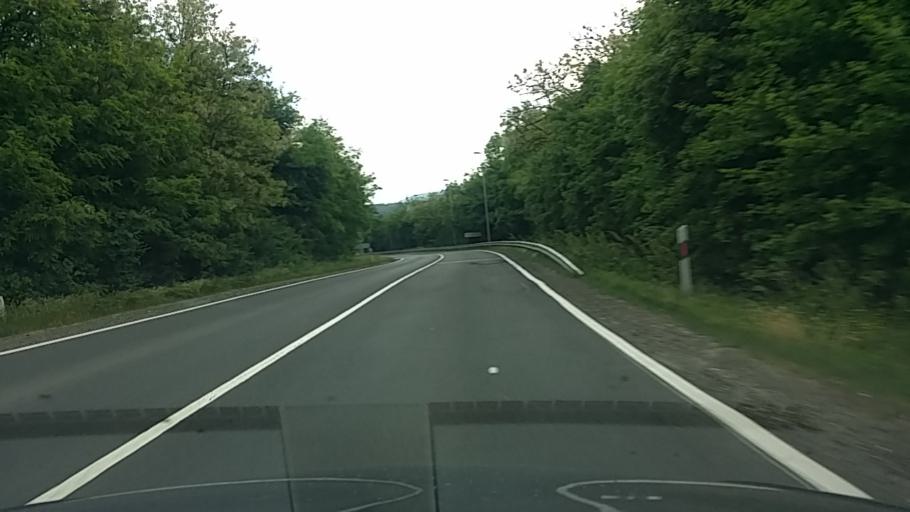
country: HU
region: Nograd
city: Nagyoroszi
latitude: 47.9805
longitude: 19.1163
